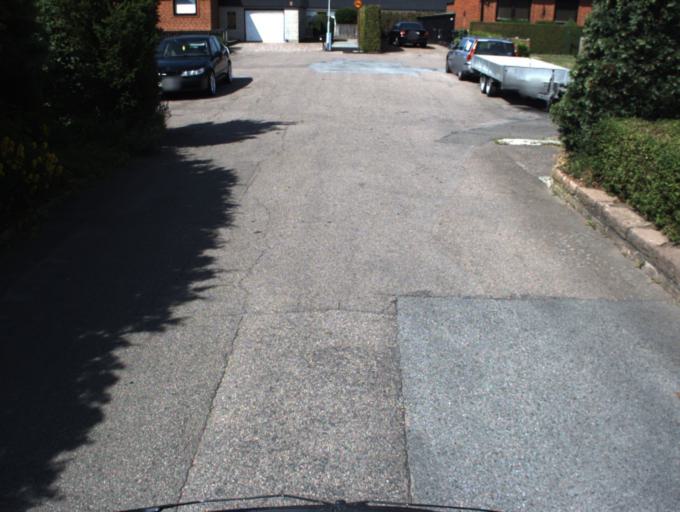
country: SE
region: Skane
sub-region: Helsingborg
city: Barslov
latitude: 56.0327
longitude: 12.8118
